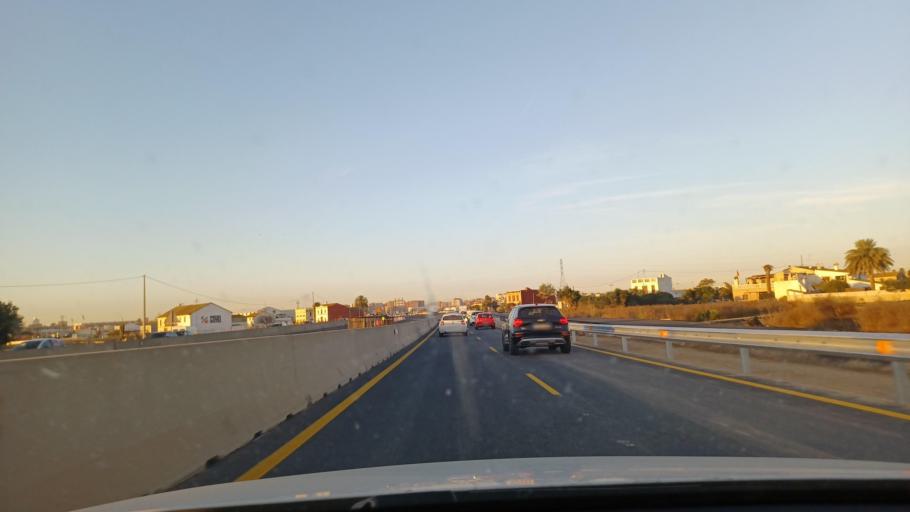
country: ES
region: Valencia
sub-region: Provincia de Valencia
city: Alboraya
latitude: 39.4937
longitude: -0.3323
